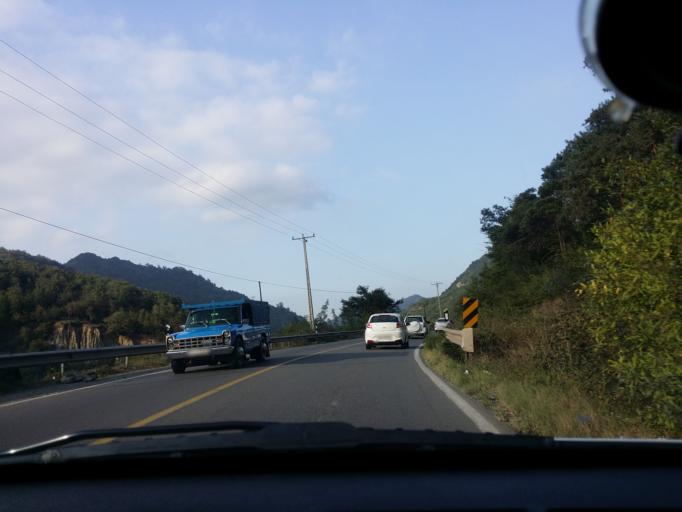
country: IR
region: Mazandaran
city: Chalus
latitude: 36.5572
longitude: 51.3727
